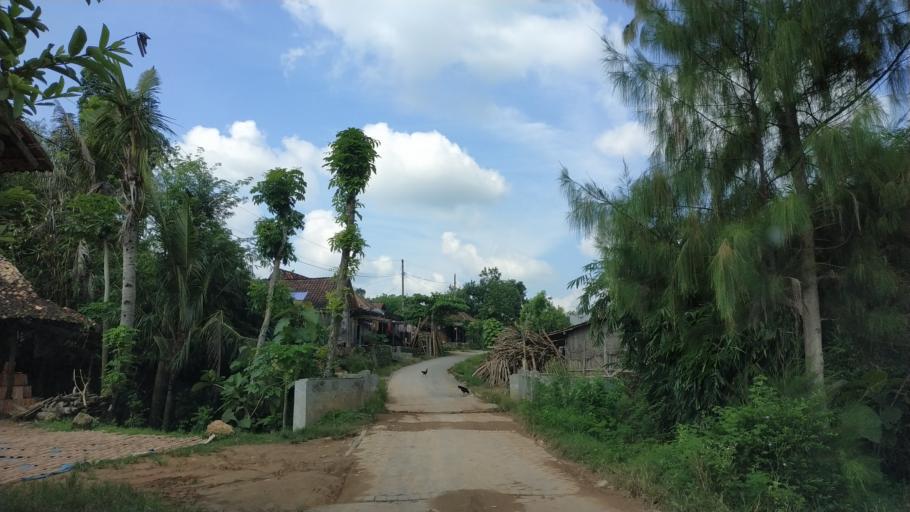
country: ID
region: Central Java
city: Guyangan
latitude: -7.0052
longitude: 111.1102
